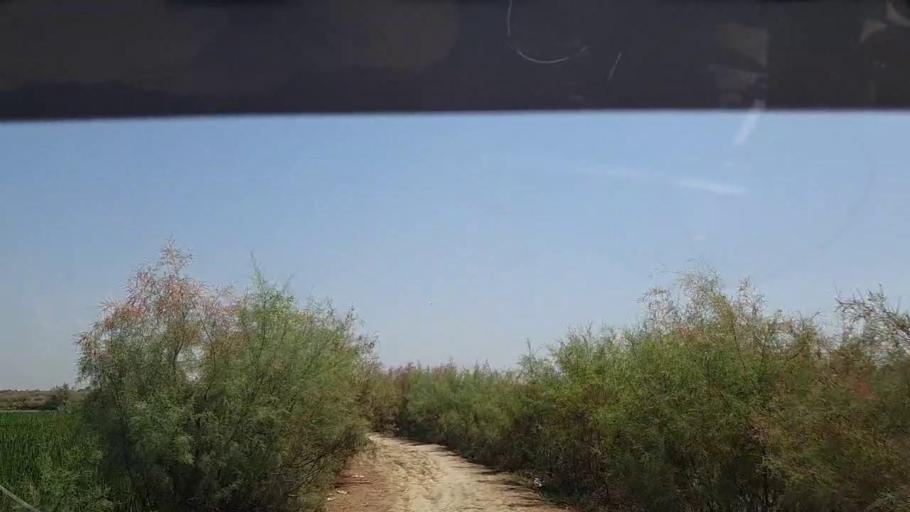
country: PK
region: Sindh
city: Ghauspur
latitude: 28.1623
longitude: 69.1420
